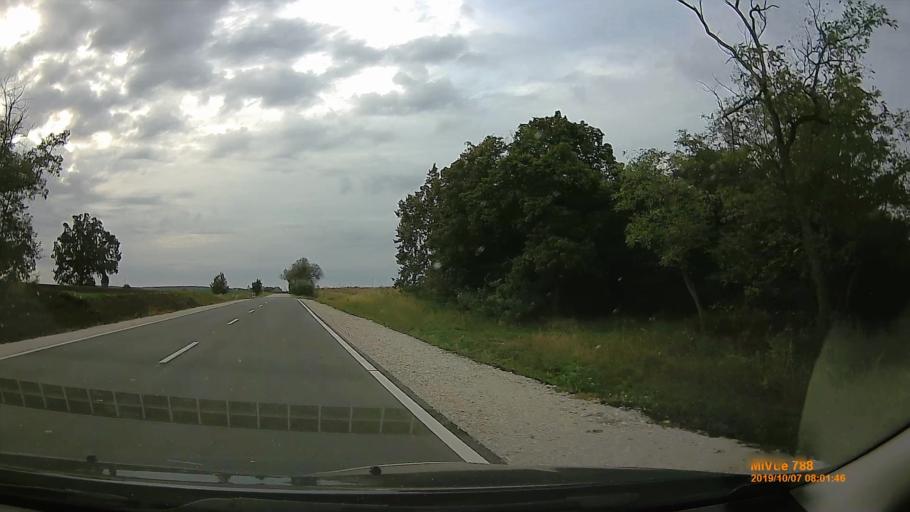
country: HU
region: Jasz-Nagykun-Szolnok
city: Cserkeszolo
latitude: 46.8760
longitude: 20.1475
